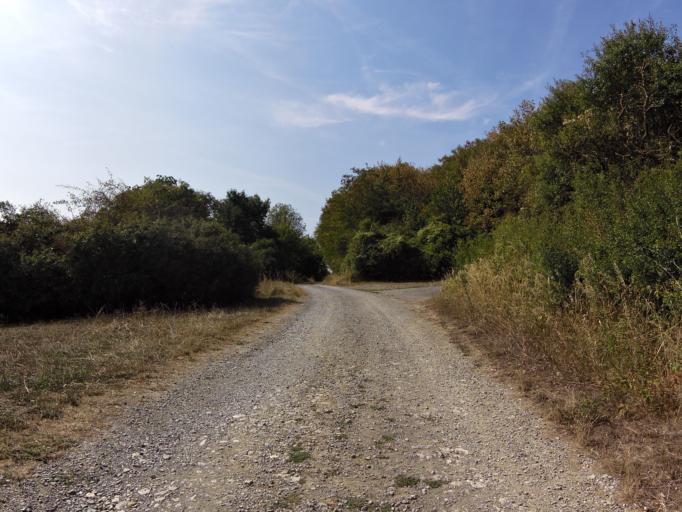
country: DE
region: Bavaria
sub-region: Regierungsbezirk Unterfranken
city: Theilheim
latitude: 49.7569
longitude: 10.0103
